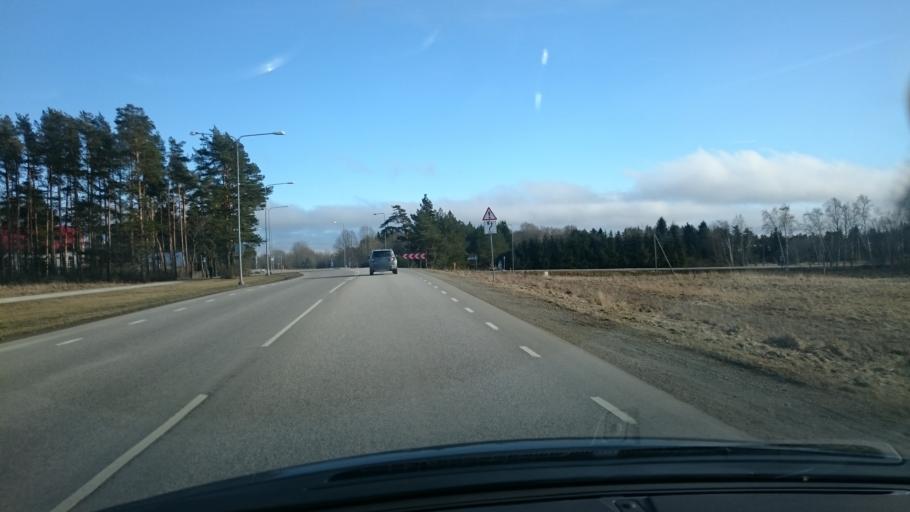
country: EE
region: Harju
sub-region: Harku vald
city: Tabasalu
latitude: 59.4391
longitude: 24.4983
